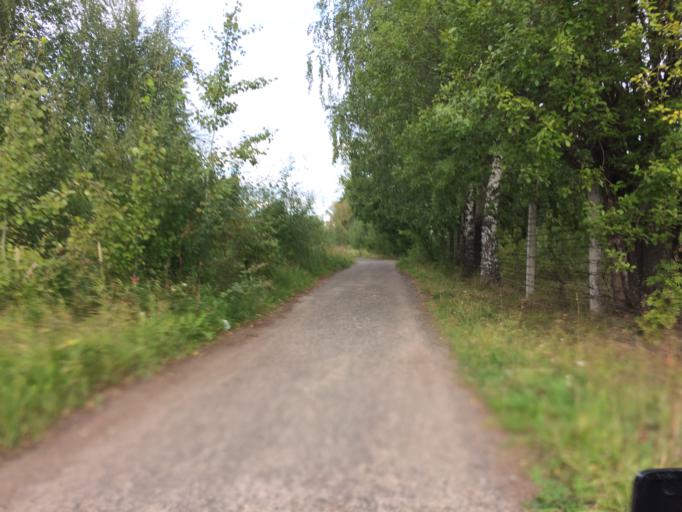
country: RU
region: Mariy-El
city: Yoshkar-Ola
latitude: 56.6598
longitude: 47.9914
